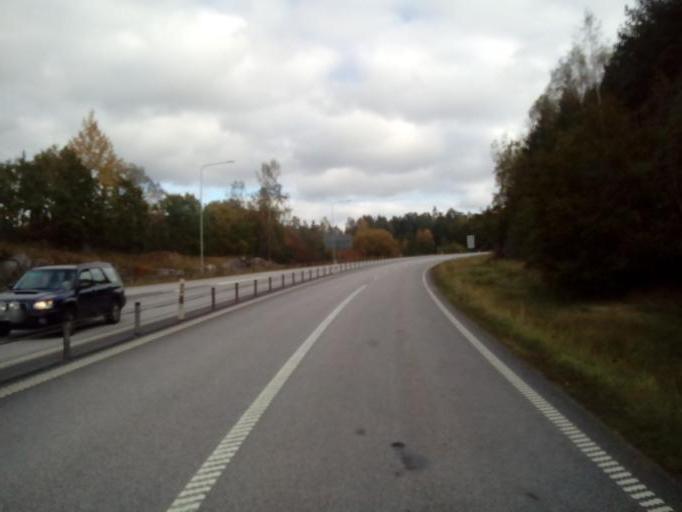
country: SE
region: Kalmar
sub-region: Vasterviks Kommun
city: Gamleby
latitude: 57.9099
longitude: 16.3871
